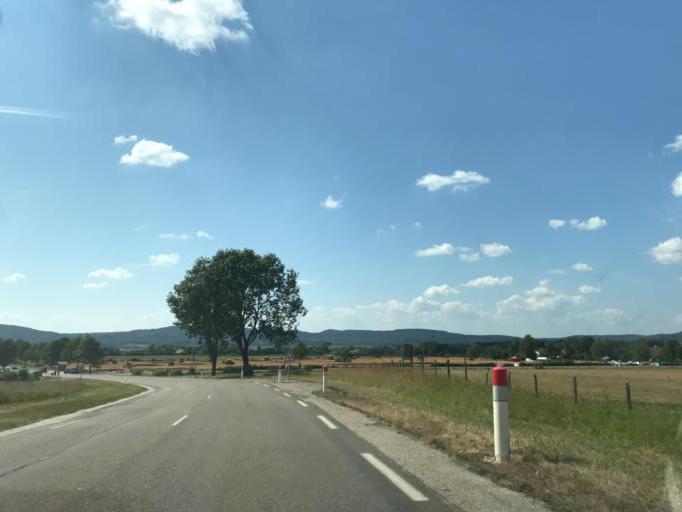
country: FR
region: Franche-Comte
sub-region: Departement du Jura
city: Clairvaux-les-Lacs
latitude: 46.5891
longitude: 5.7327
